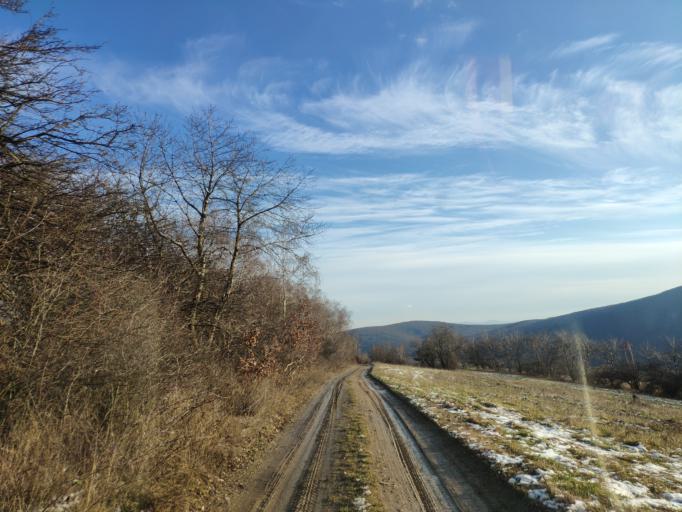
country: SK
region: Kosicky
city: Moldava nad Bodvou
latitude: 48.7370
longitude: 21.0906
